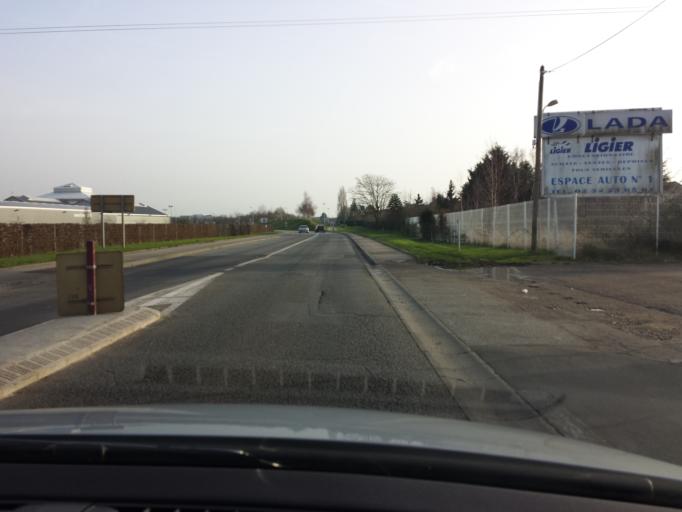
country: FR
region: Haute-Normandie
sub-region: Departement de l'Eure
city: Evreux
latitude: 49.0083
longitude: 1.1681
